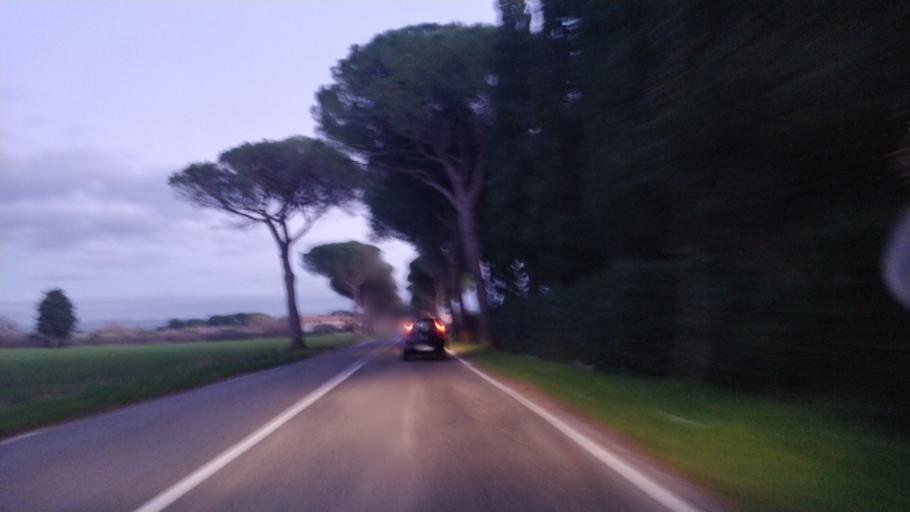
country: IT
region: Tuscany
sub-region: Provincia di Livorno
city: S.P. in Palazzi
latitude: 43.3341
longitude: 10.4929
